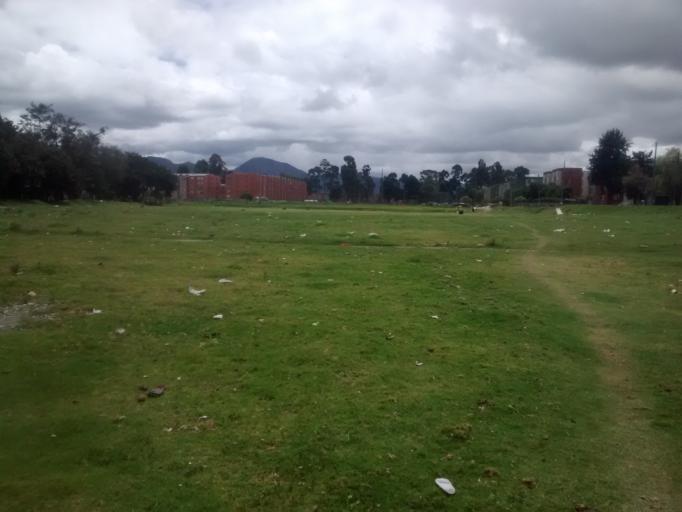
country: CO
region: Cundinamarca
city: Cota
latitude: 4.7452
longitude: -74.1061
